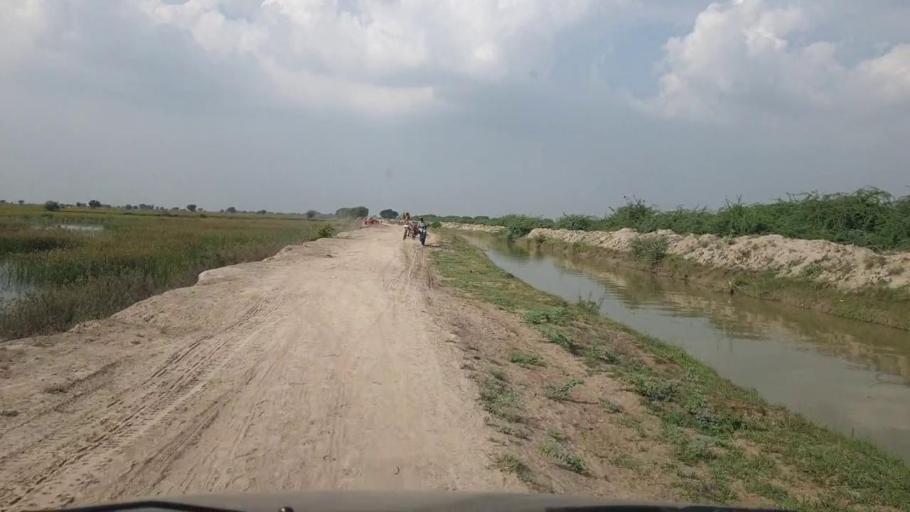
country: PK
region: Sindh
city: Badin
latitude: 24.5710
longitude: 68.6321
